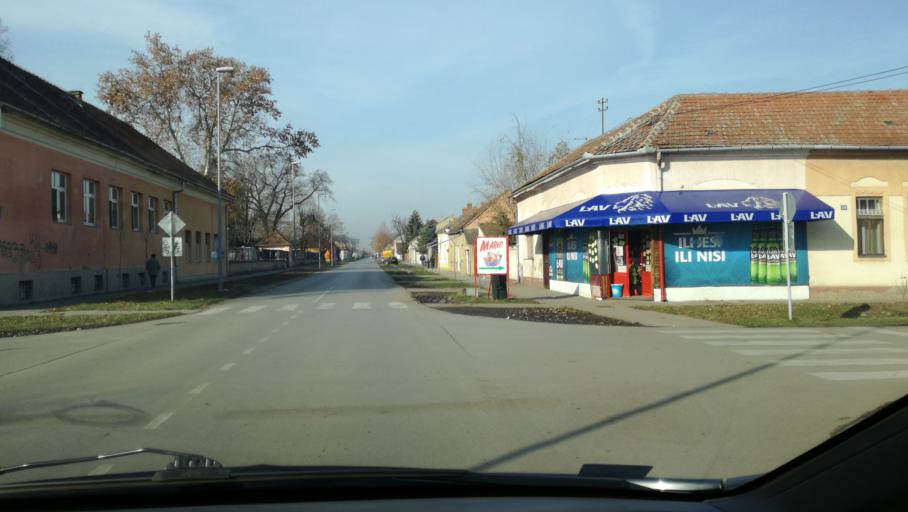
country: RS
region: Autonomna Pokrajina Vojvodina
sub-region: Severnobanatski Okrug
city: Kikinda
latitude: 45.8331
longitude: 20.4810
